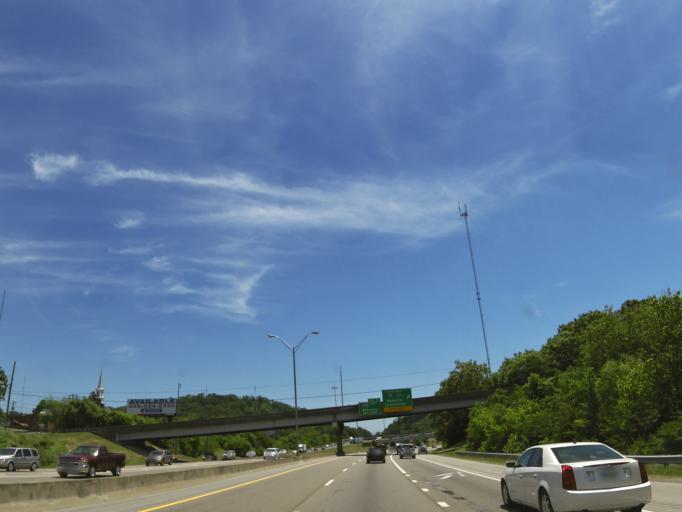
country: US
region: Tennessee
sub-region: Knox County
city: Knoxville
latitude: 36.0043
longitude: -83.9634
